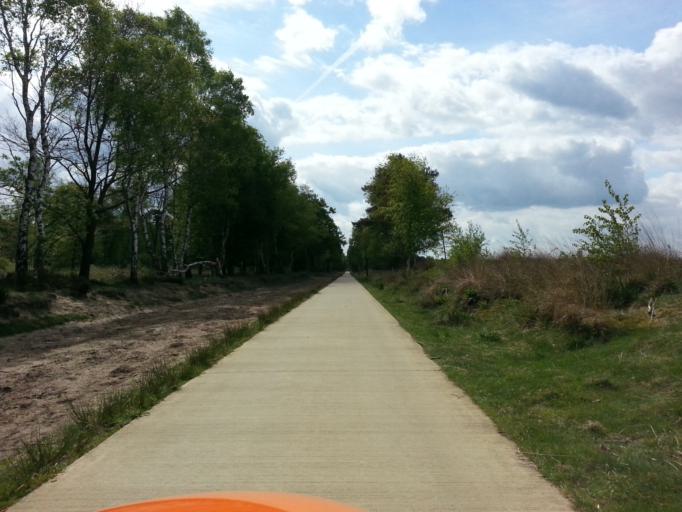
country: NL
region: Gelderland
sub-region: Gemeente Renkum
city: Heelsum
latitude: 52.0285
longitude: 5.7408
